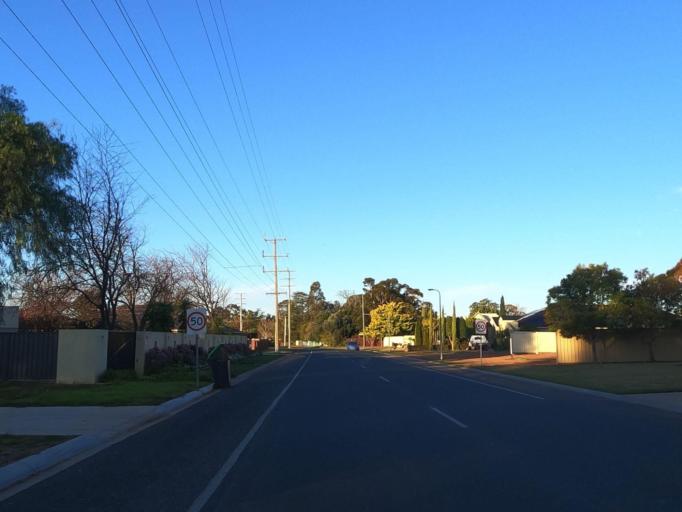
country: AU
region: Victoria
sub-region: Swan Hill
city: Swan Hill
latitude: -35.3603
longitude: 143.5555
